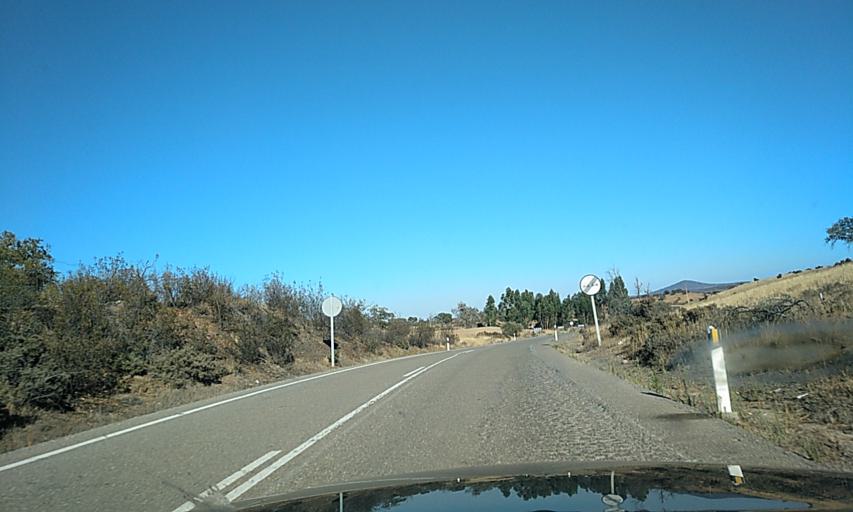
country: ES
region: Andalusia
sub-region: Provincia de Huelva
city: Santa Barbara de Casa
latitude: 37.7887
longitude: -7.1700
